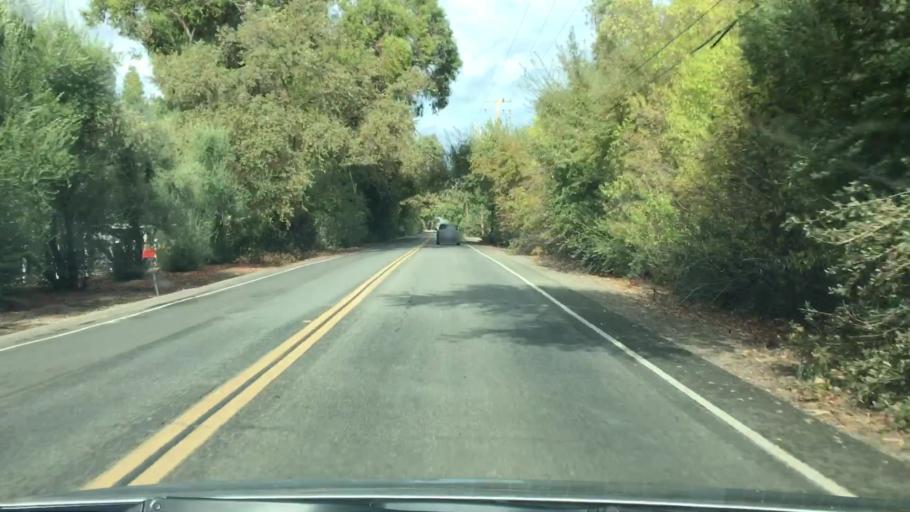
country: US
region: California
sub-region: Yolo County
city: Davis
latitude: 38.5510
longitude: -121.8033
